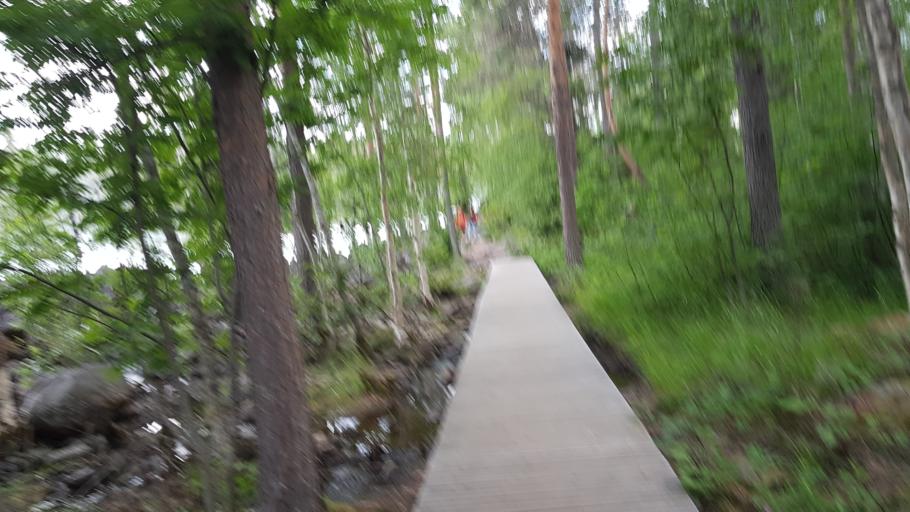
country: SE
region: Norrbotten
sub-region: Alvsbyns Kommun
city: AElvsbyn
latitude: 65.8538
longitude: 20.4135
